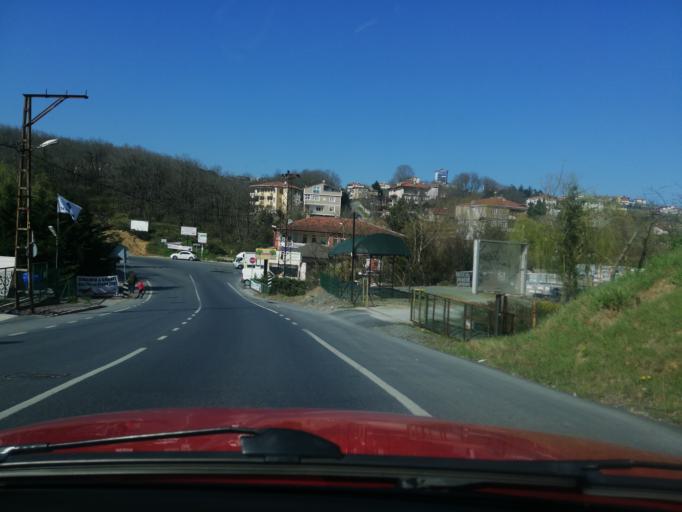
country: TR
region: Istanbul
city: Umraniye
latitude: 41.0786
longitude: 29.1450
